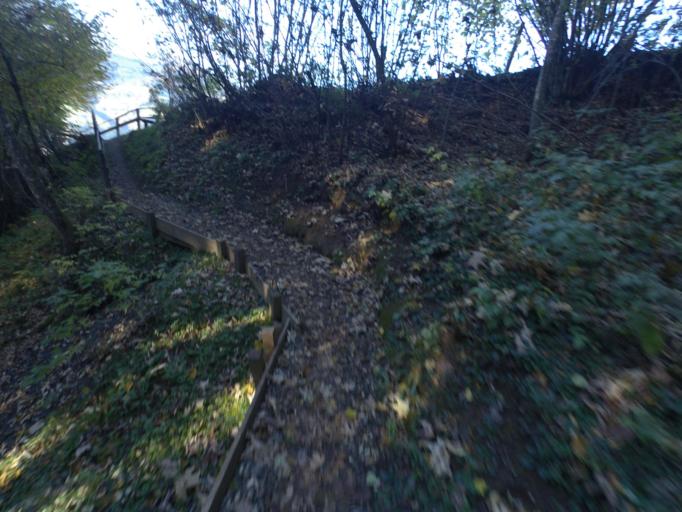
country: AT
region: Salzburg
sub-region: Politischer Bezirk Sankt Johann im Pongau
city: Sankt Johann im Pongau
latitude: 47.3451
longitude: 13.2209
